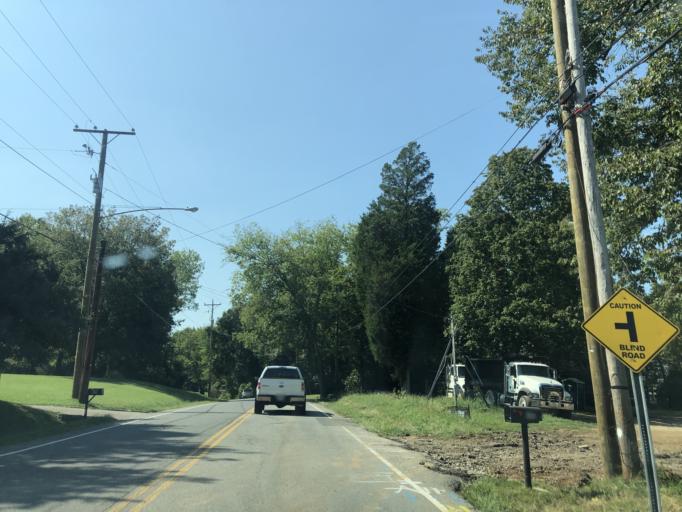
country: US
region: Tennessee
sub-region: Davidson County
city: Oak Hill
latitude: 36.0877
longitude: -86.7810
